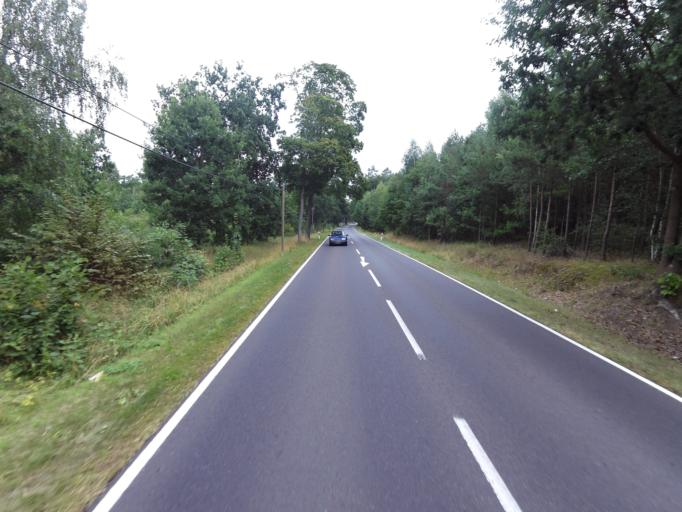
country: DE
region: Brandenburg
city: Liebenwalde
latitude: 52.8852
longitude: 13.3965
